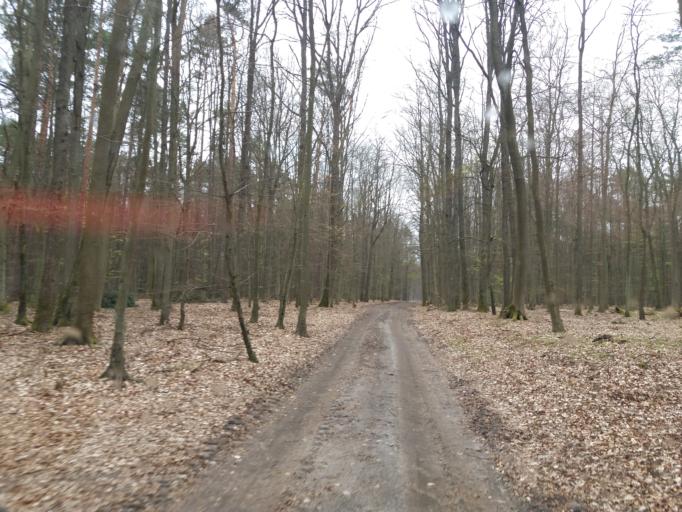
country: PL
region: West Pomeranian Voivodeship
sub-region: Powiat choszczenski
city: Drawno
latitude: 53.0978
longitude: 15.8398
